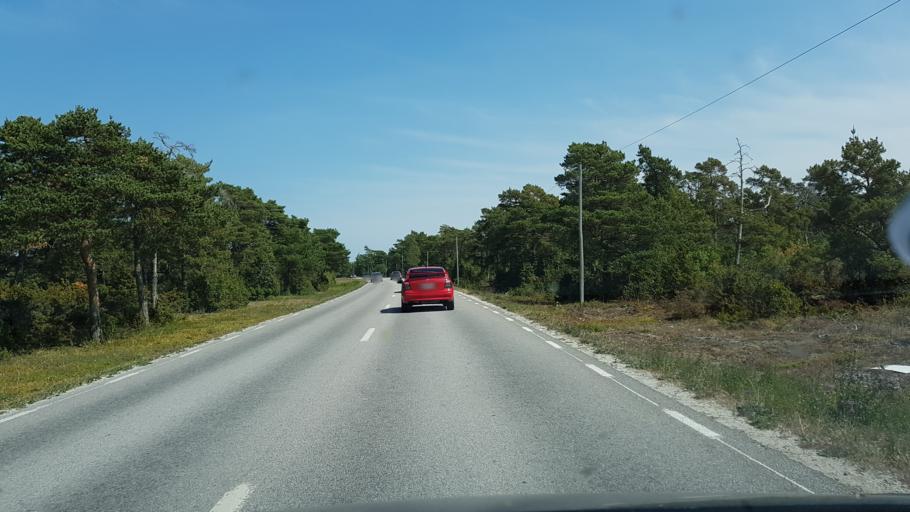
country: SE
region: Gotland
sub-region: Gotland
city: Visby
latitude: 57.6303
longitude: 18.4274
